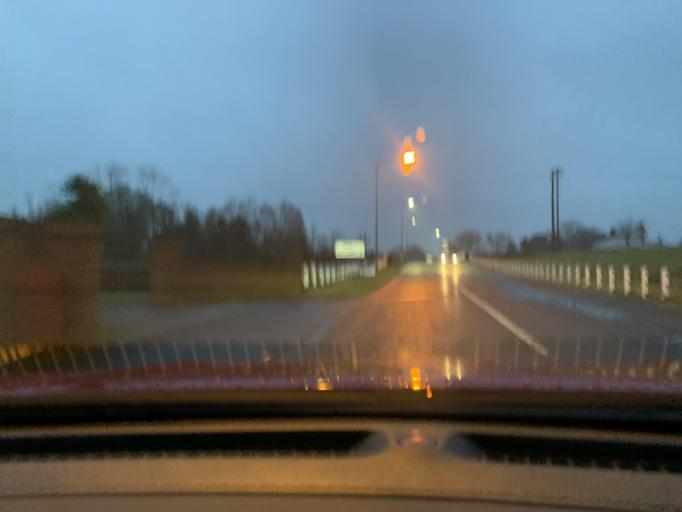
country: IE
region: Connaught
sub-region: Sligo
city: Ballymote
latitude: 53.9977
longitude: -8.5218
